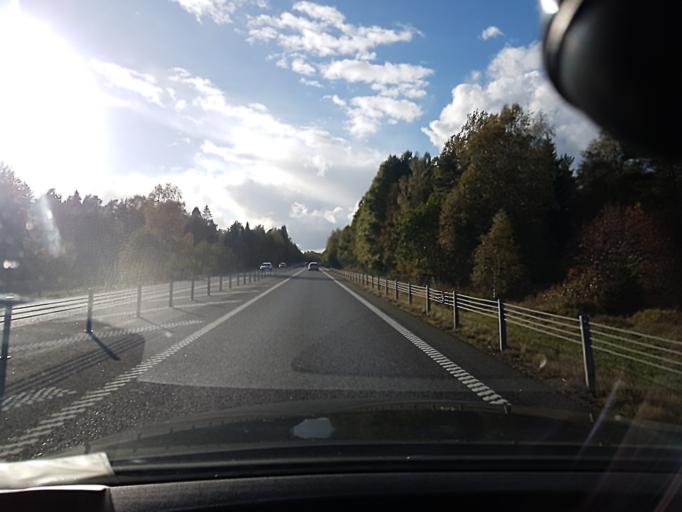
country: SE
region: Kronoberg
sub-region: Ljungby Kommun
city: Lagan
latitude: 56.8515
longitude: 14.0416
